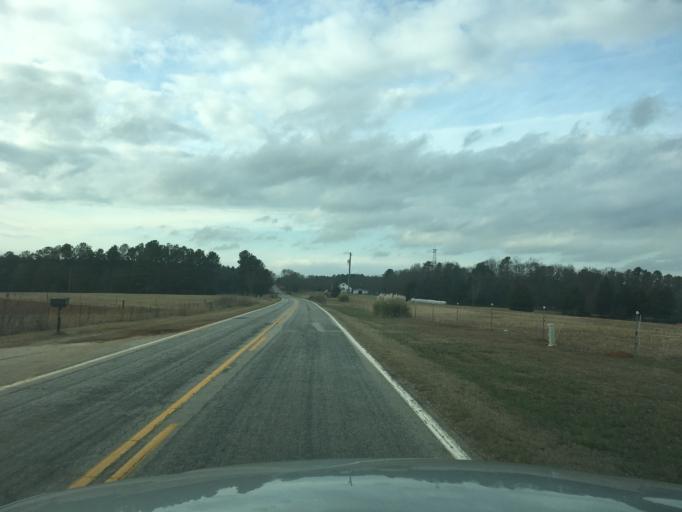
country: US
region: South Carolina
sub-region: Abbeville County
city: Due West
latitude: 34.3208
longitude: -82.4674
